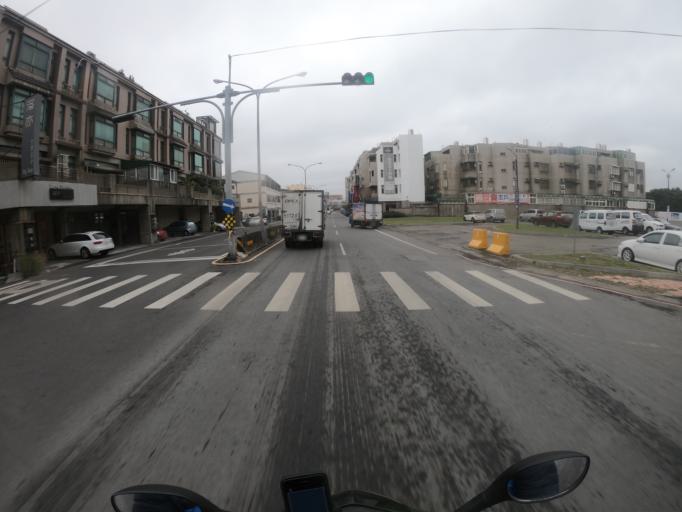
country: TW
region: Taiwan
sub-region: Hsinchu
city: Zhubei
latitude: 24.8262
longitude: 121.0049
